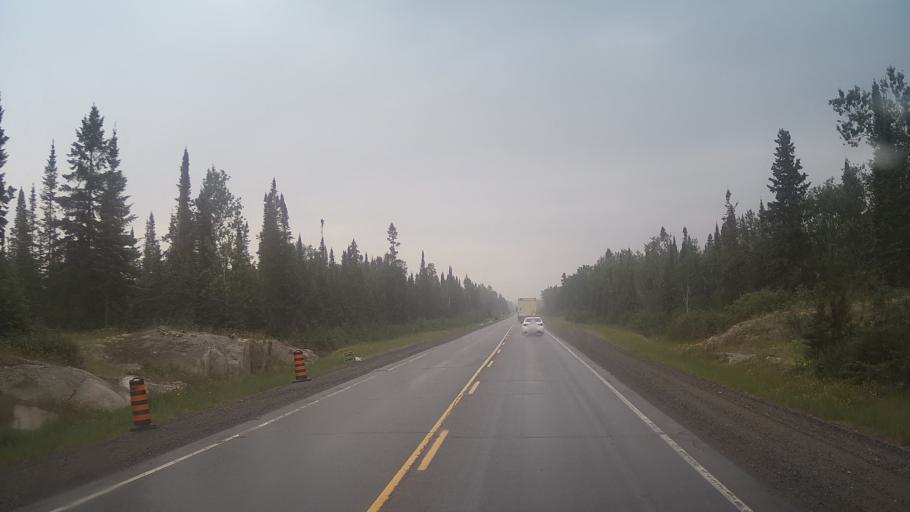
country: CA
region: Ontario
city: Greenstone
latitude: 49.1786
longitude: -88.2245
